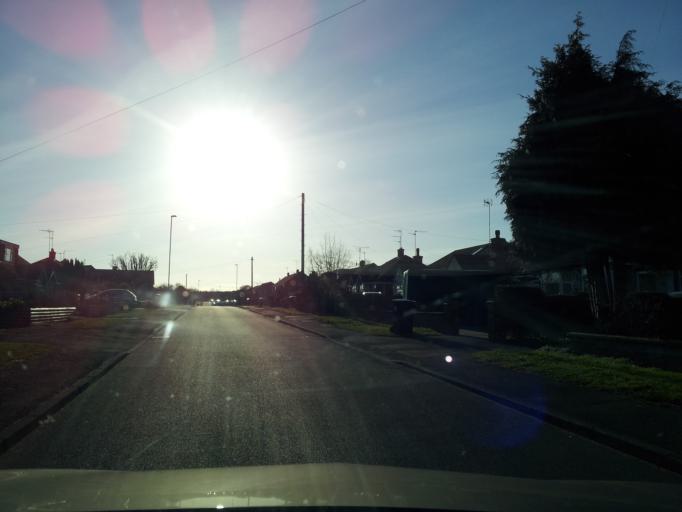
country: GB
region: England
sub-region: Northamptonshire
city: Northampton
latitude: 52.2566
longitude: -0.9555
